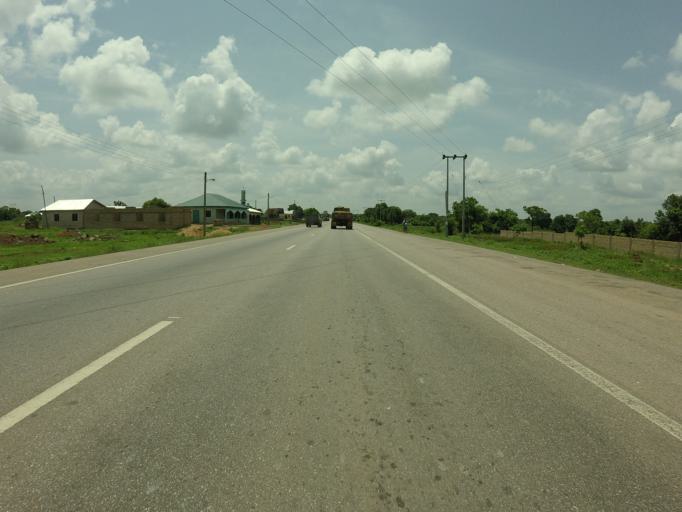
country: GH
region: Northern
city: Tamale
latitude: 9.1529
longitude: -1.1427
